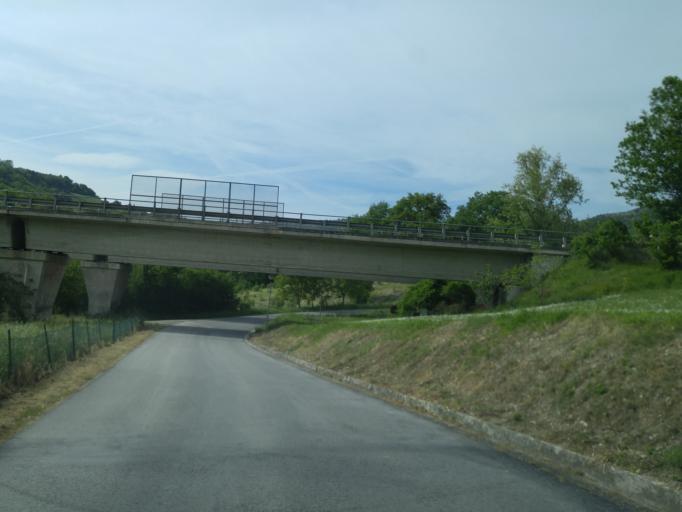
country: IT
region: The Marches
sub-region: Provincia di Pesaro e Urbino
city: Acqualagna
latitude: 43.6369
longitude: 12.6902
